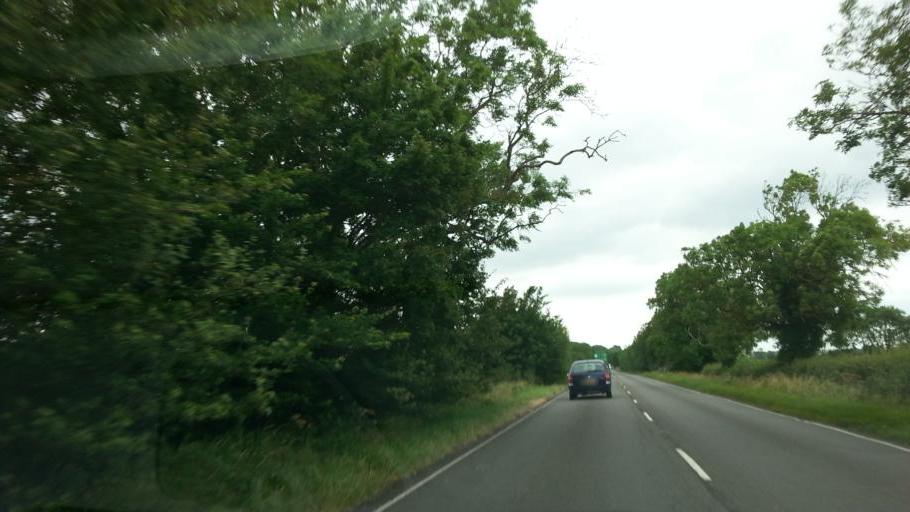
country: GB
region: England
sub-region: Cambridgeshire
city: Papworth Everard
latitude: 52.2685
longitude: -0.1321
